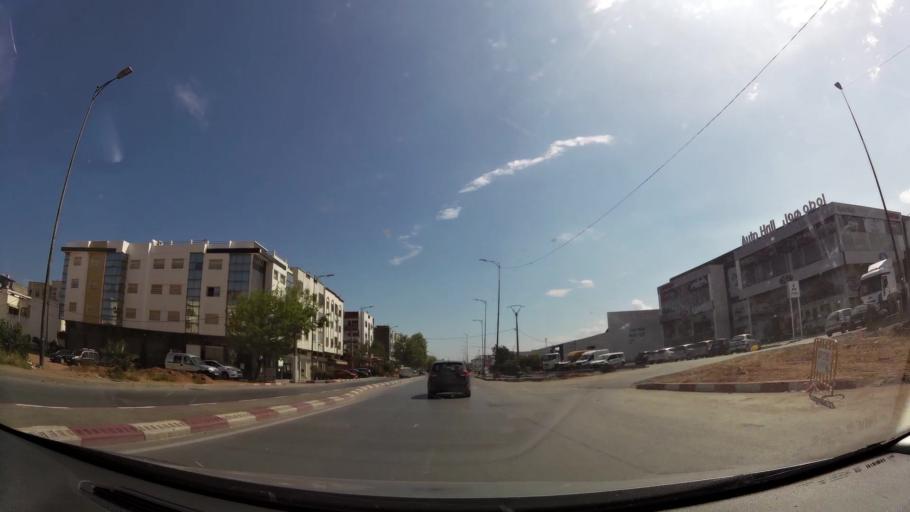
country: MA
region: Rabat-Sale-Zemmour-Zaer
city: Sale
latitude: 34.0637
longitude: -6.7981
